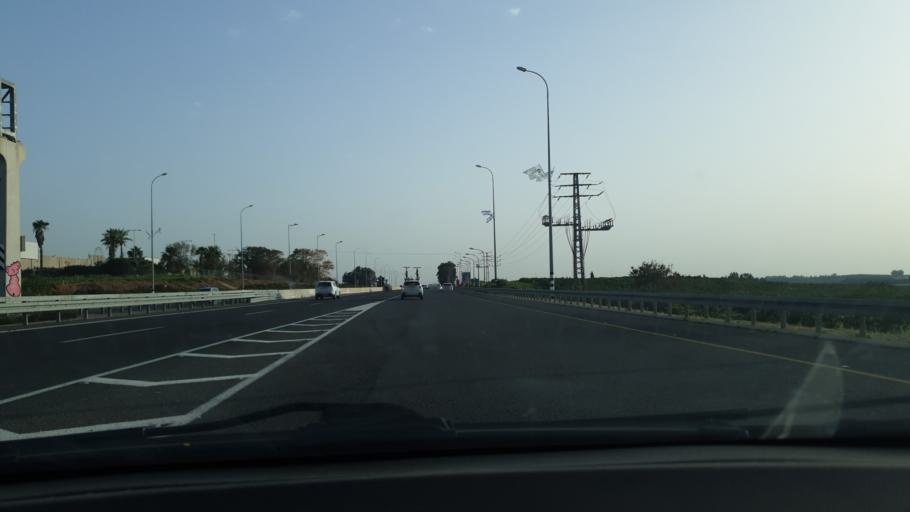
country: IL
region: Central District
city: Even Yehuda
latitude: 32.2514
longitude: 34.8899
